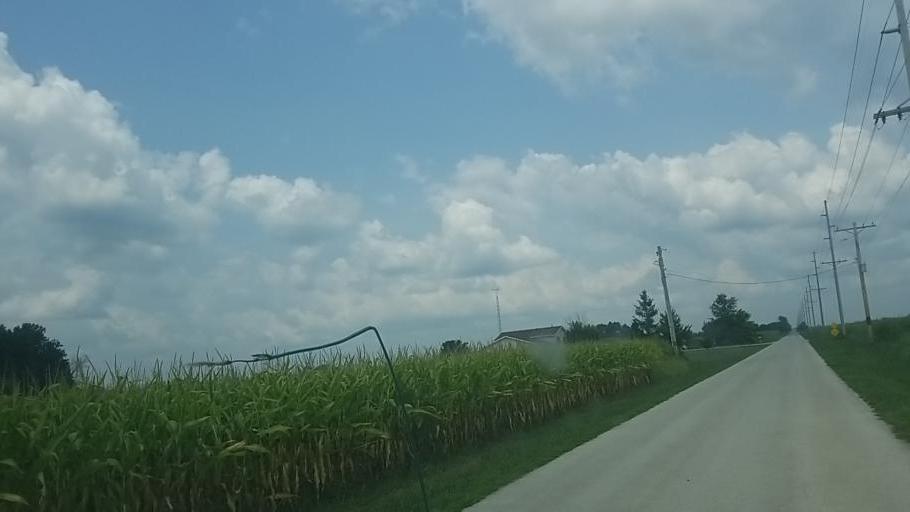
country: US
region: Ohio
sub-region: Wyandot County
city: Carey
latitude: 40.9686
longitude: -83.3049
